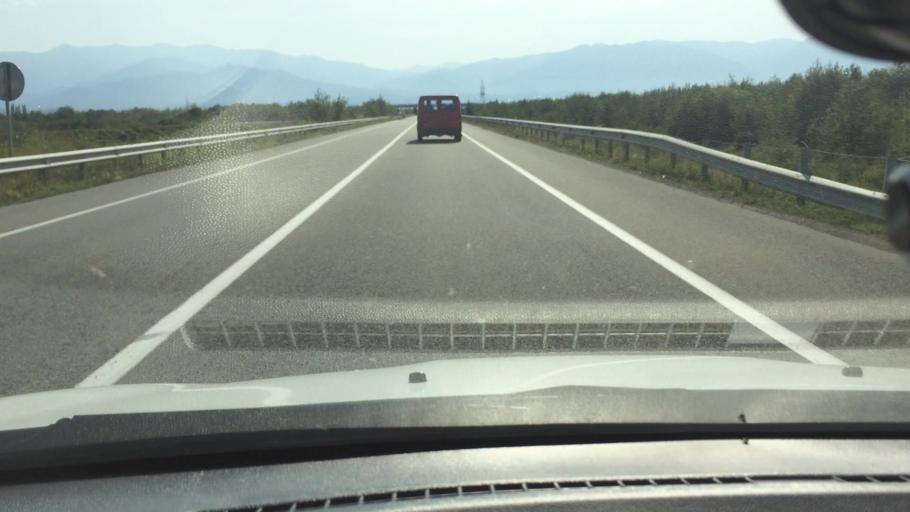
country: GE
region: Ajaria
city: Ochkhamuri
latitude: 41.8968
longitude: 41.7994
